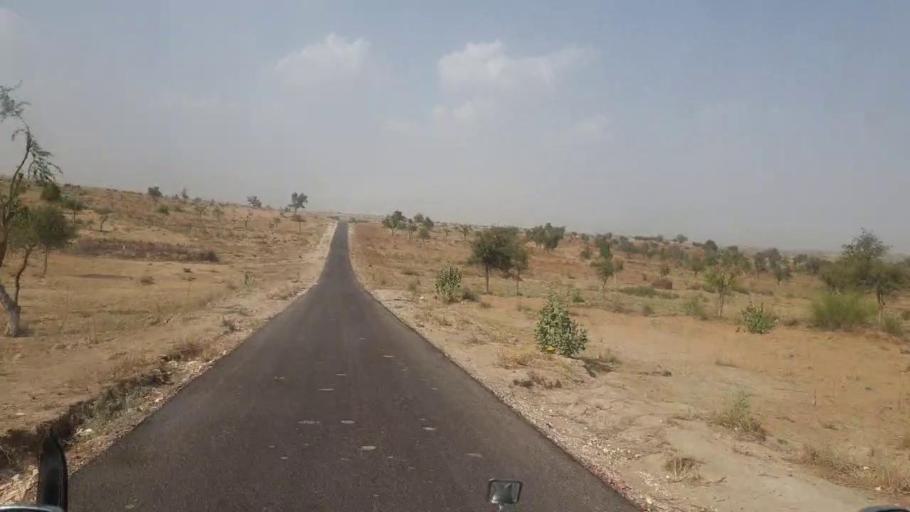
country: PK
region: Sindh
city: Islamkot
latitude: 25.1946
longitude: 70.2849
